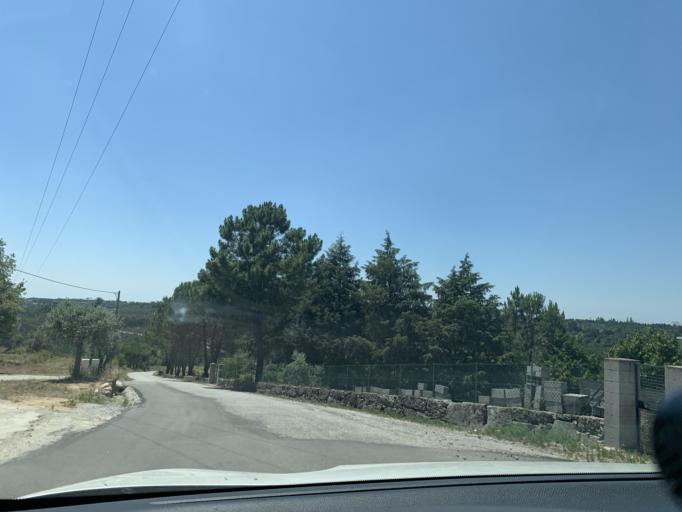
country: PT
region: Viseu
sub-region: Mangualde
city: Mangualde
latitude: 40.5558
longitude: -7.7295
